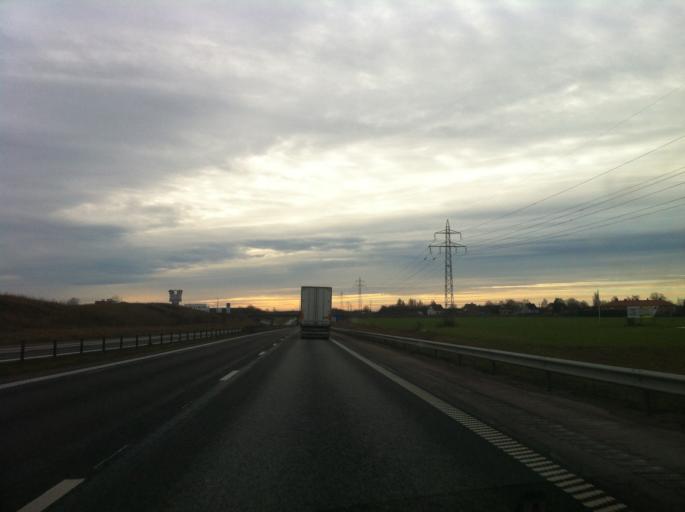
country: SE
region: Skane
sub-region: Astorps Kommun
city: Astorp
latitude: 56.1314
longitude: 12.9171
